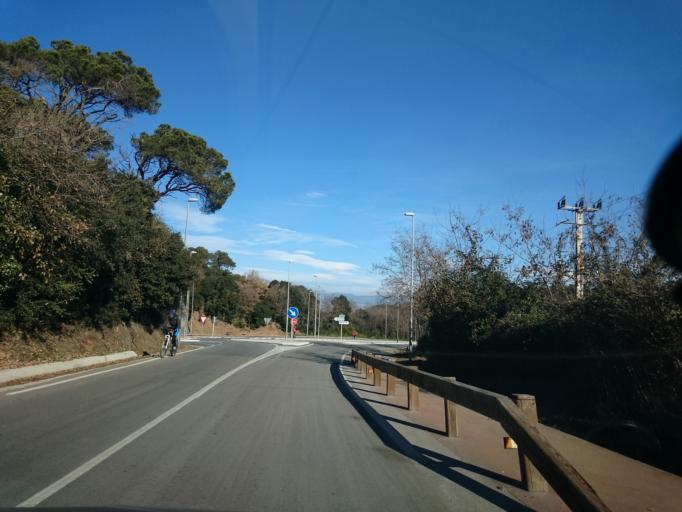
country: ES
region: Catalonia
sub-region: Provincia de Barcelona
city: Sarria-Sant Gervasi
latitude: 41.4283
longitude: 2.1232
